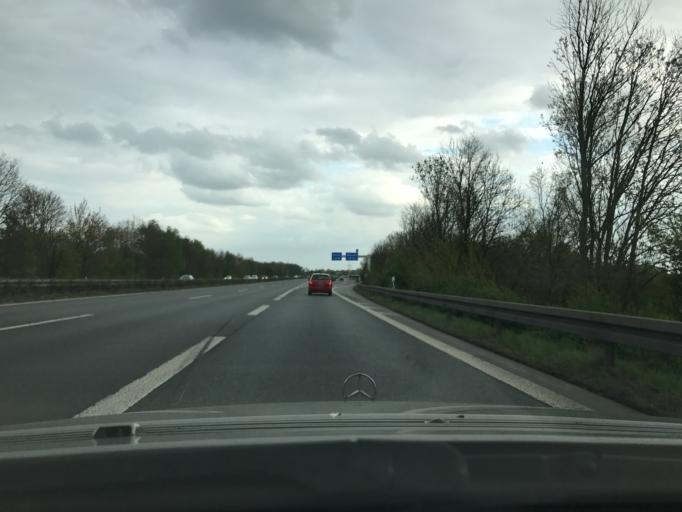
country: DE
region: North Rhine-Westphalia
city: Lunen
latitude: 51.5827
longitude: 7.4900
